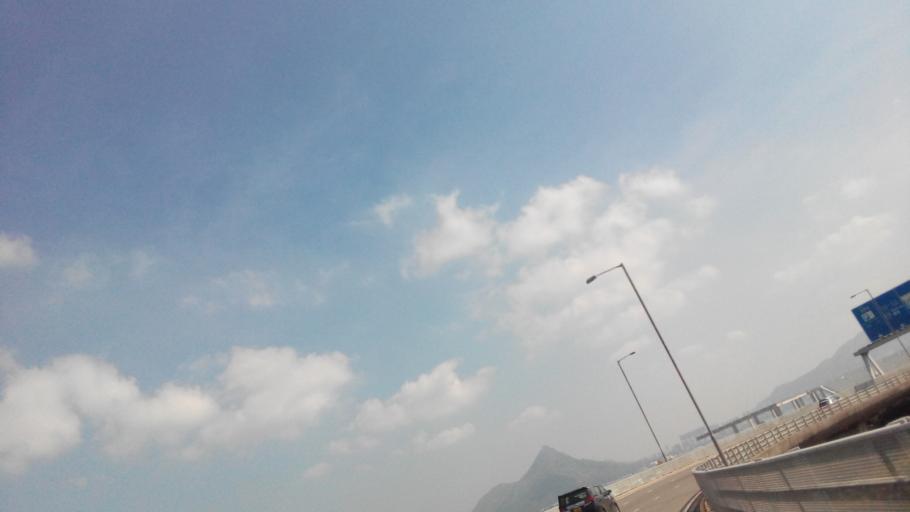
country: HK
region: Tuen Mun
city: Tuen Mun
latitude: 22.3189
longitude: 113.9352
